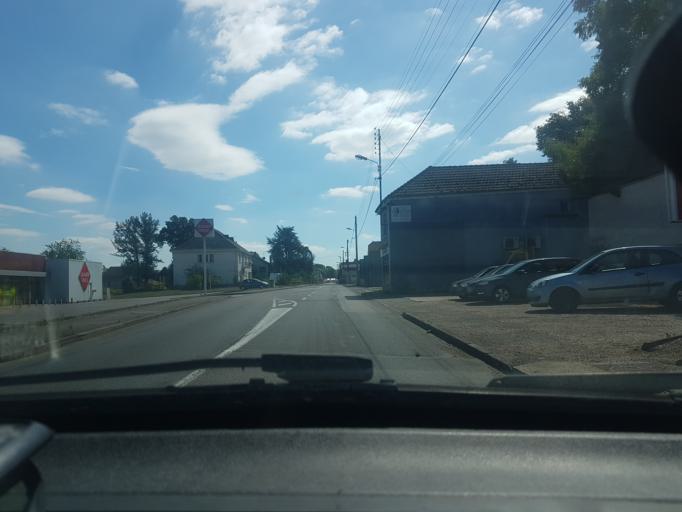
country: FR
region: Franche-Comte
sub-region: Departement de la Haute-Saone
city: Gray
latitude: 47.4446
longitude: 5.5982
